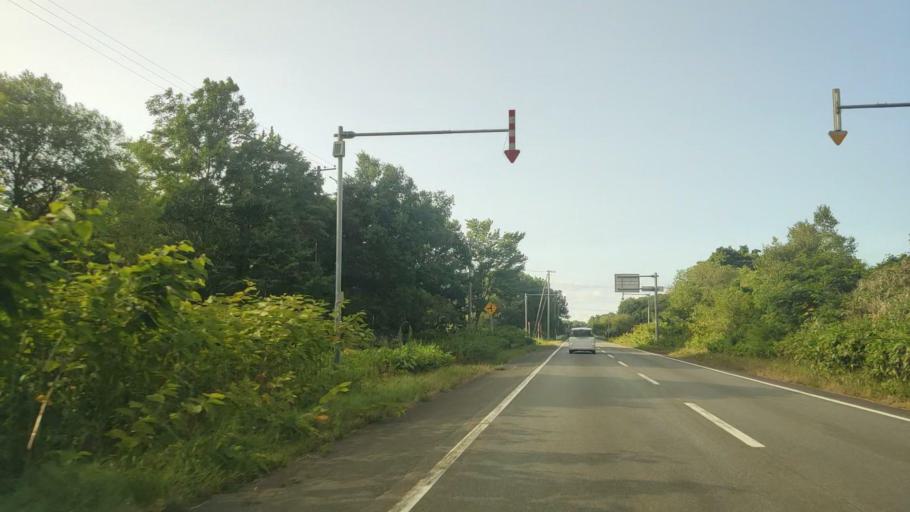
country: JP
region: Hokkaido
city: Makubetsu
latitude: 45.0606
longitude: 141.7484
